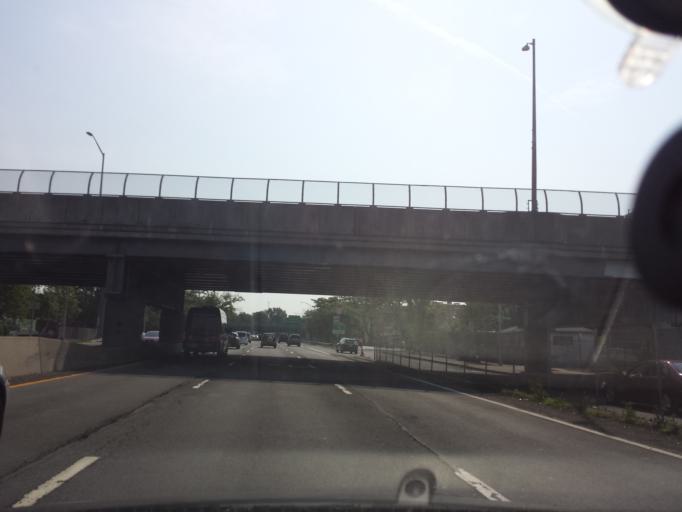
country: US
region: New York
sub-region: Kings County
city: Coney Island
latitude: 40.5845
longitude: -73.9607
